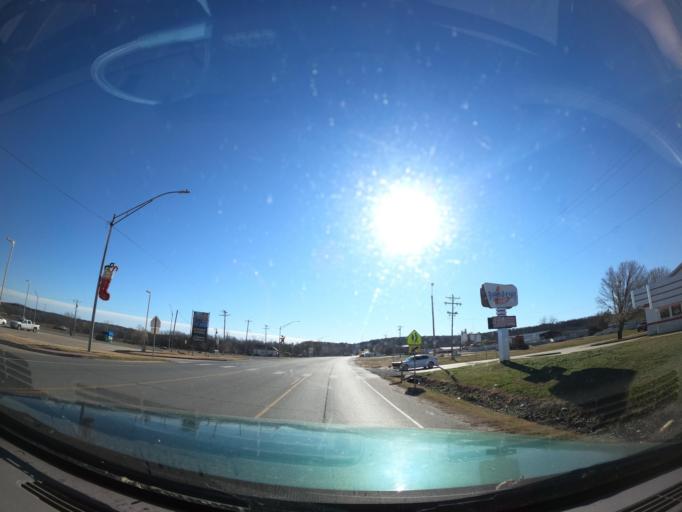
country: US
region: Oklahoma
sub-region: McIntosh County
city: Eufaula
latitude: 35.2788
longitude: -95.5833
